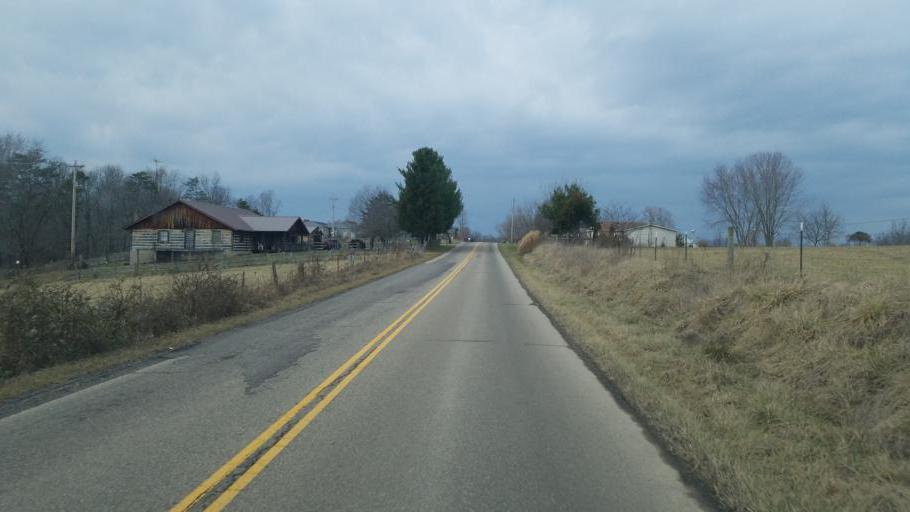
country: US
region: Ohio
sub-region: Gallia County
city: Gallipolis
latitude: 38.7818
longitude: -82.3900
